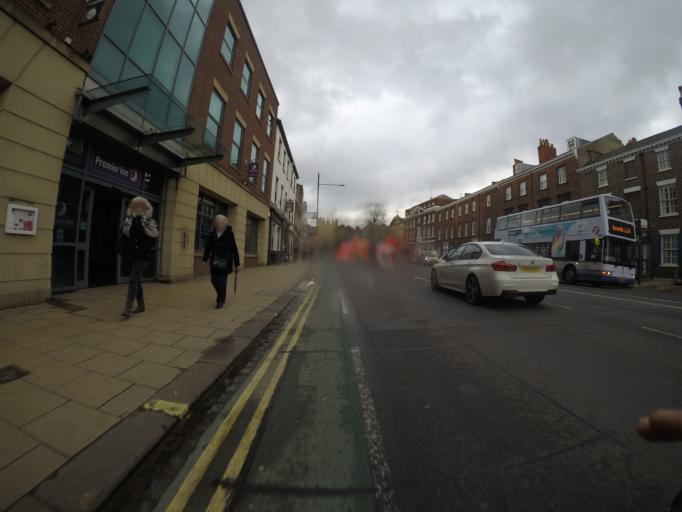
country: GB
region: England
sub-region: City of York
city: York
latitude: 53.9550
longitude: -1.0923
